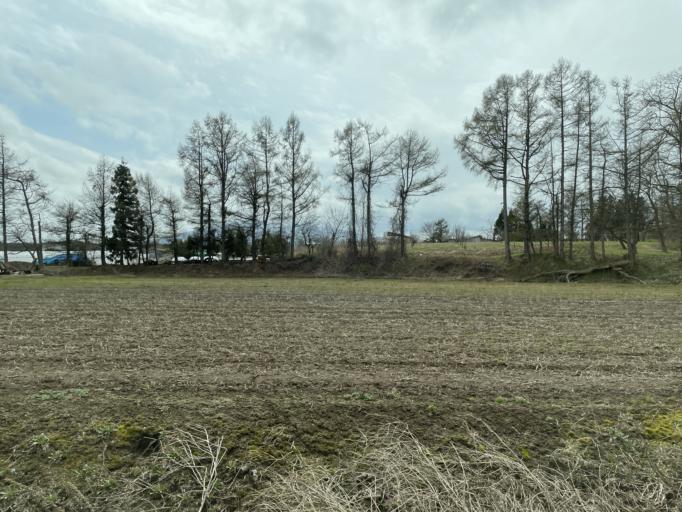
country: JP
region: Aomori
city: Shimokizukuri
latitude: 40.7868
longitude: 140.3027
